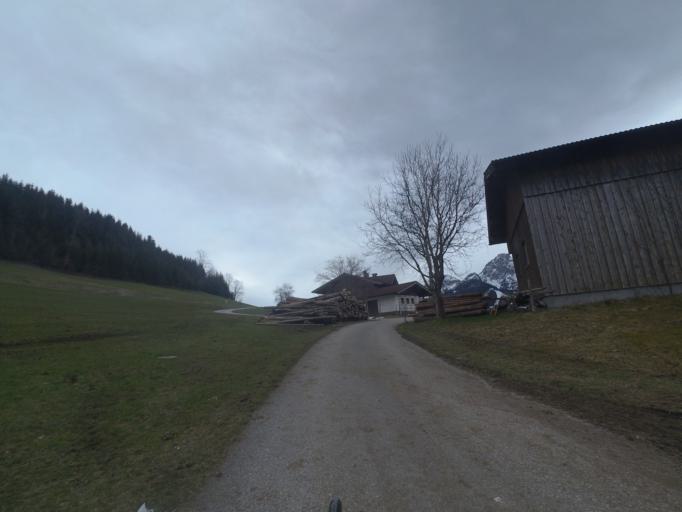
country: AT
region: Salzburg
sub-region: Politischer Bezirk Hallein
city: Abtenau
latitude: 47.5803
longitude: 13.3290
